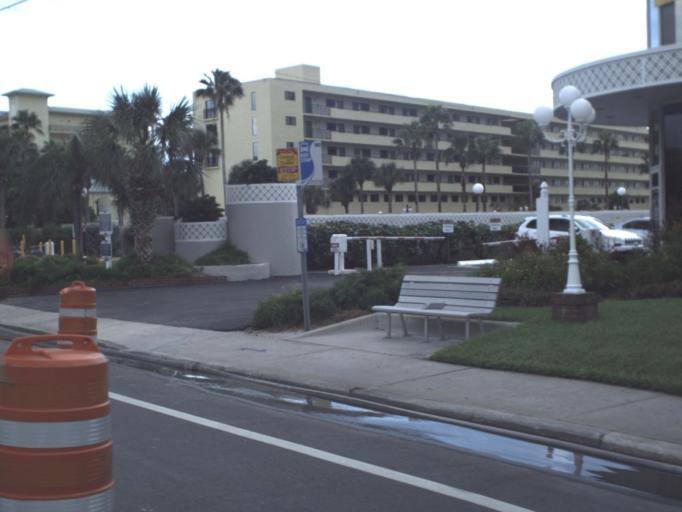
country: US
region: Florida
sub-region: Pinellas County
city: Saint Pete Beach
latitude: 27.7290
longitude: -82.7431
